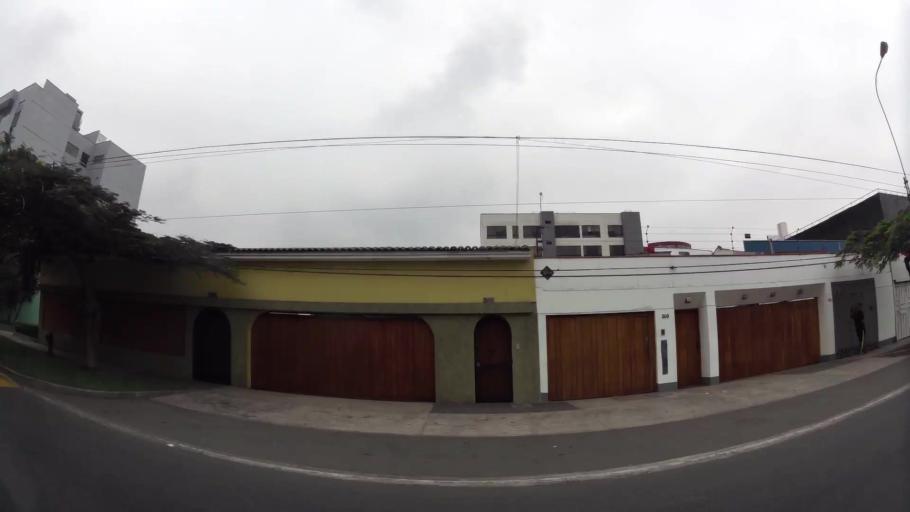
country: PE
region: Lima
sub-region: Lima
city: San Luis
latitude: -12.0961
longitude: -77.0128
